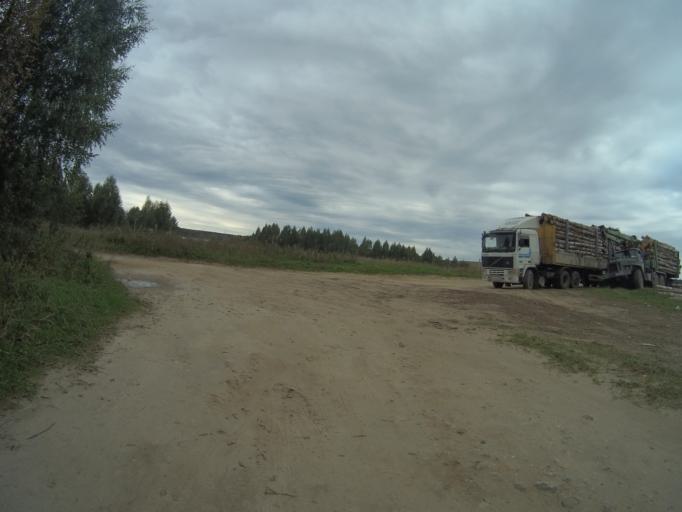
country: RU
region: Vladimir
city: Golovino
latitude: 55.9745
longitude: 40.4593
